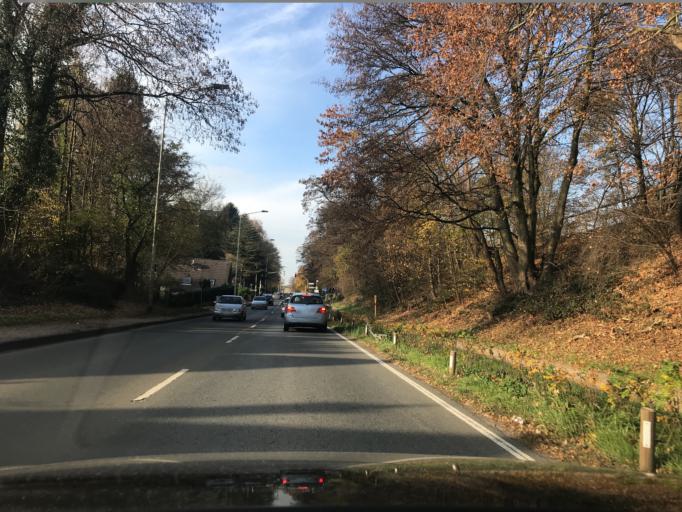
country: DE
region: North Rhine-Westphalia
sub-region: Regierungsbezirk Dusseldorf
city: Solingen
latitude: 51.1838
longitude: 7.0635
